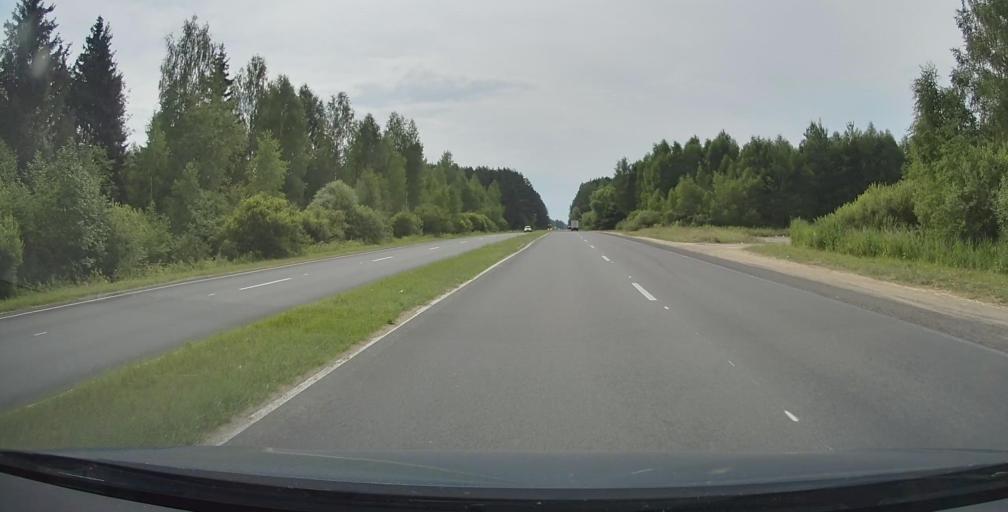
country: RU
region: Jaroslavl
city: Rybinsk
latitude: 58.0199
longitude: 38.9660
